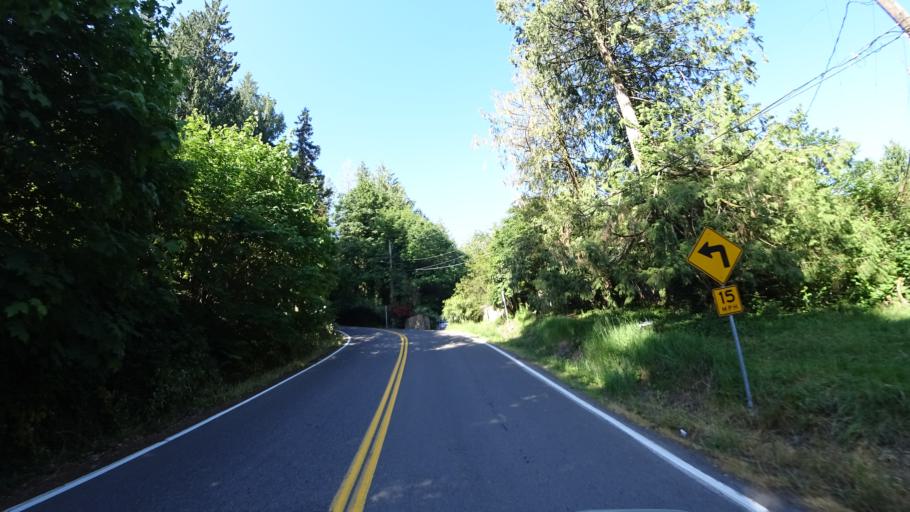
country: US
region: Oregon
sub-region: Clackamas County
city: Happy Valley
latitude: 45.4733
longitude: -122.5370
